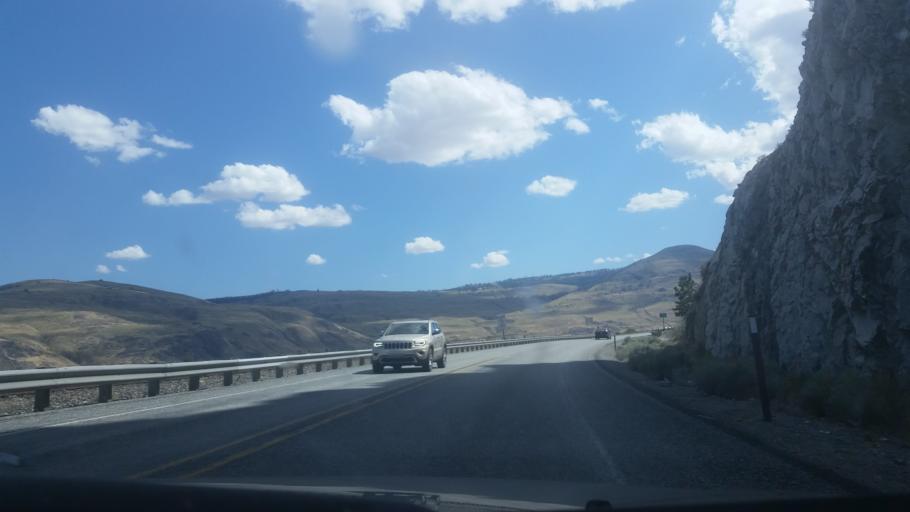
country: US
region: Washington
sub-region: Okanogan County
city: Brewster
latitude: 47.9620
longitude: -119.8766
